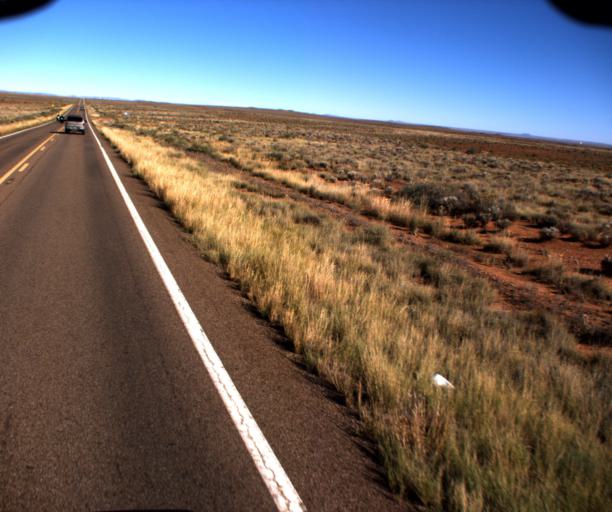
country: US
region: Arizona
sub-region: Navajo County
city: Holbrook
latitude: 34.7623
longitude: -110.1252
